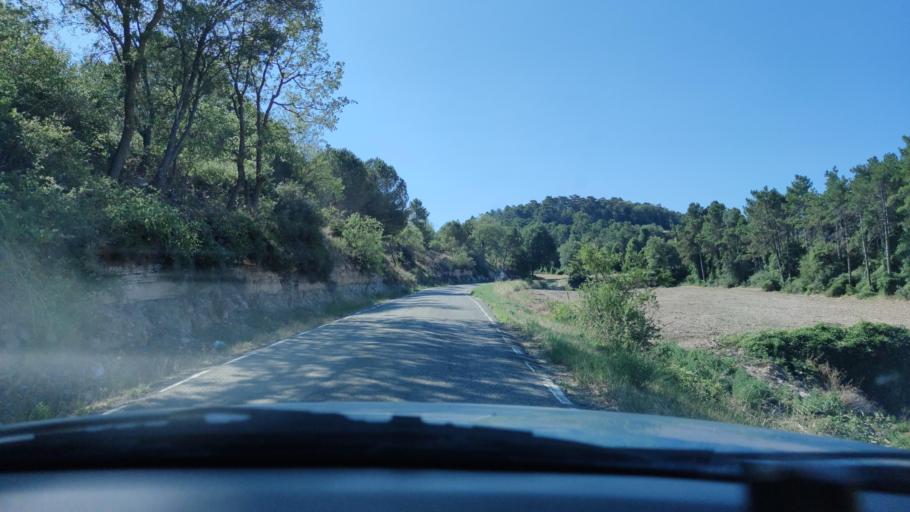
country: ES
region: Catalonia
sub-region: Provincia de Lleida
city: Sant Guim de Freixenet
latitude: 41.6749
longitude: 1.4055
